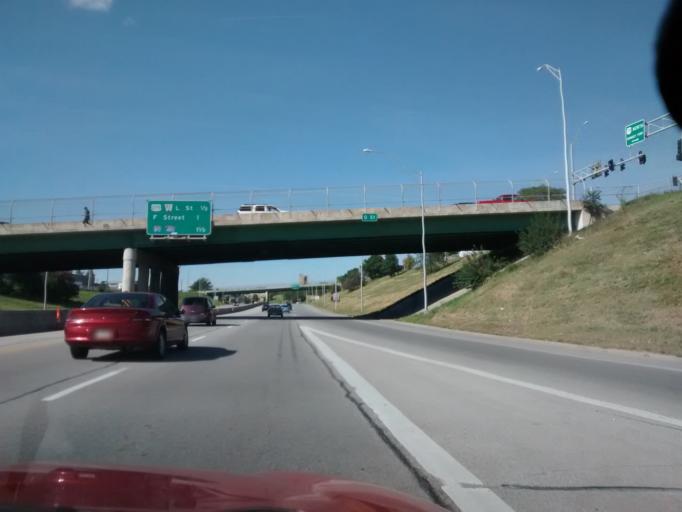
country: US
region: Nebraska
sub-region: Douglas County
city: Omaha
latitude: 41.2050
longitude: -95.9492
